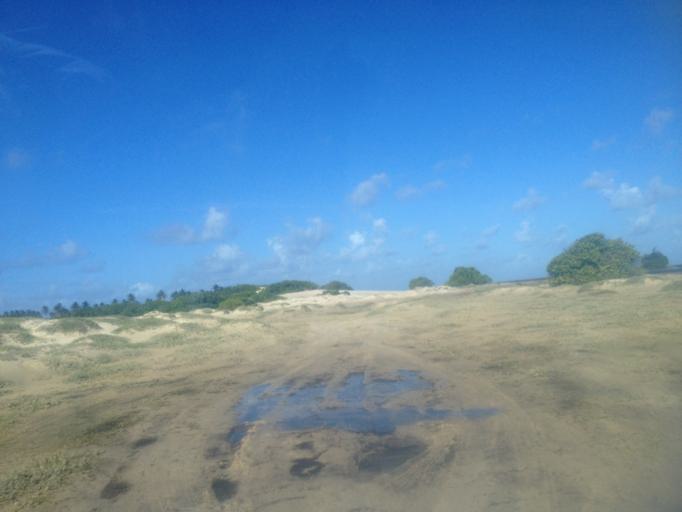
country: BR
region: Sergipe
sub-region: Indiaroba
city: Indiaroba
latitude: -11.4752
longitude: -37.3702
